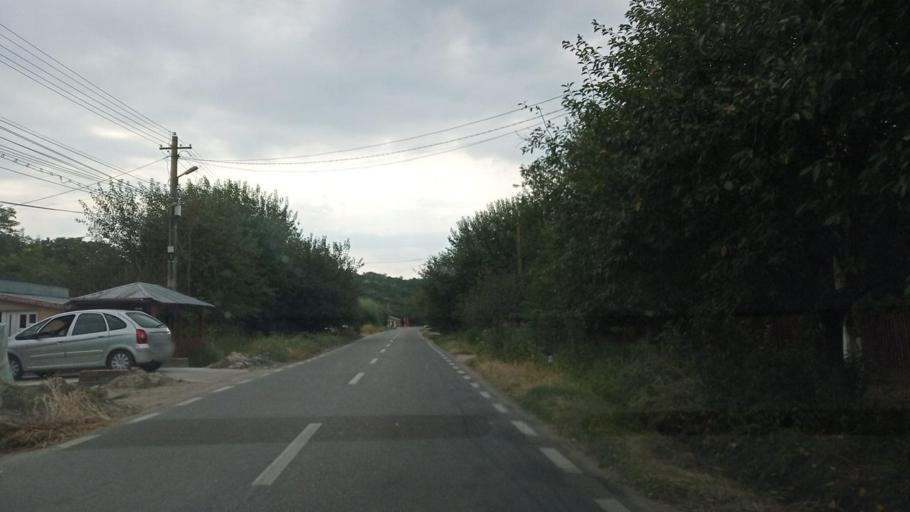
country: RO
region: Giurgiu
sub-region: Comuna Izvoarele
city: Isvoarele
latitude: 44.1721
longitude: 26.3337
